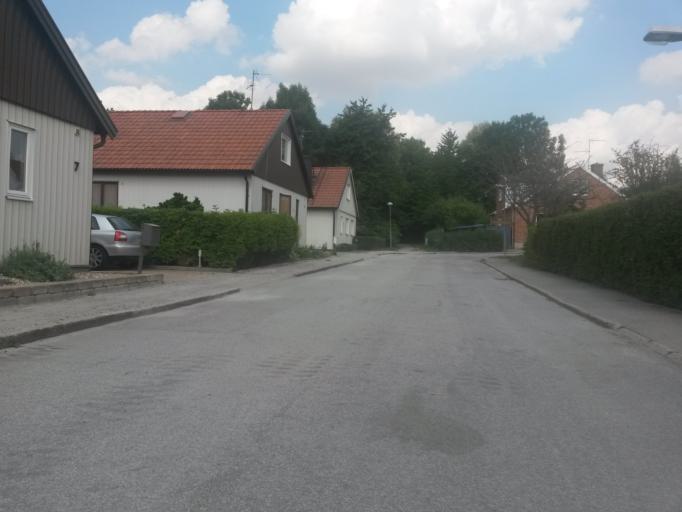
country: SE
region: Skane
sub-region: Lunds Kommun
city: Lund
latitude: 55.7022
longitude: 13.2333
